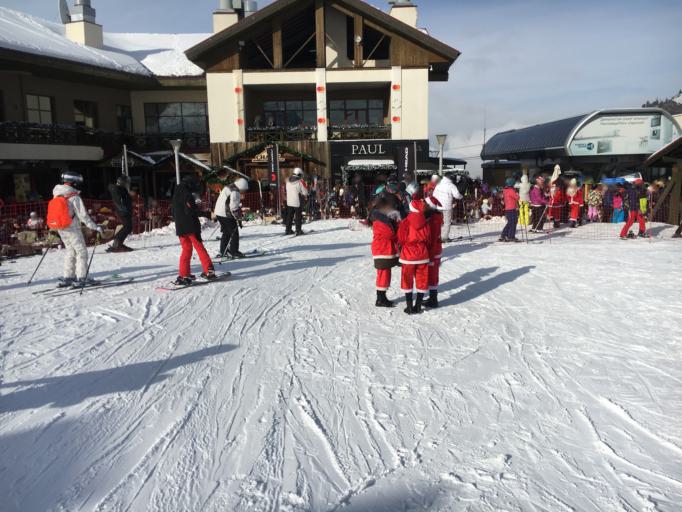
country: KZ
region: Almaty Qalasy
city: Almaty
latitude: 43.1274
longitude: 77.0808
